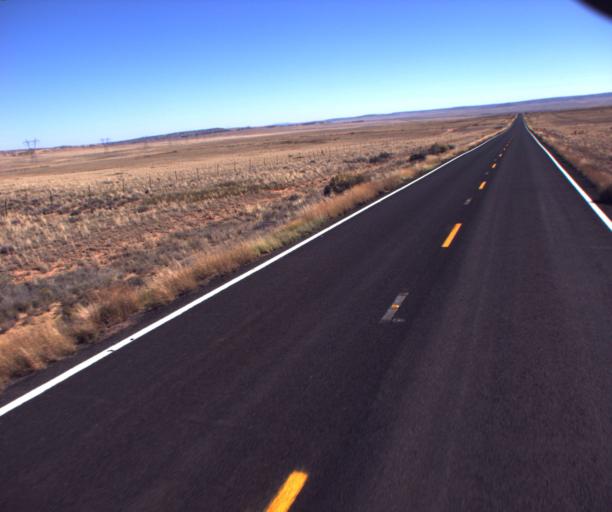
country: US
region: Arizona
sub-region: Coconino County
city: Tuba City
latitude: 35.9715
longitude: -110.8344
